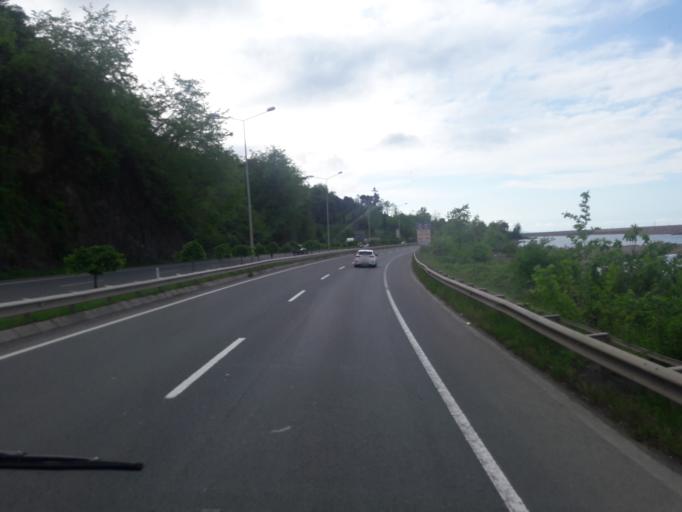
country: TR
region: Giresun
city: Piraziz
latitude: 40.9580
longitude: 38.1111
